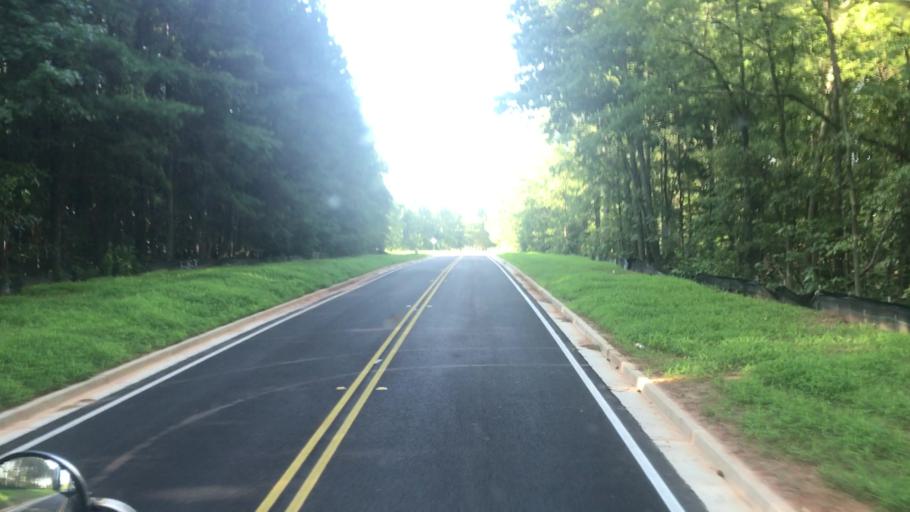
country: US
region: Georgia
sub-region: Henry County
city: McDonough
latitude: 33.3949
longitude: -84.1685
